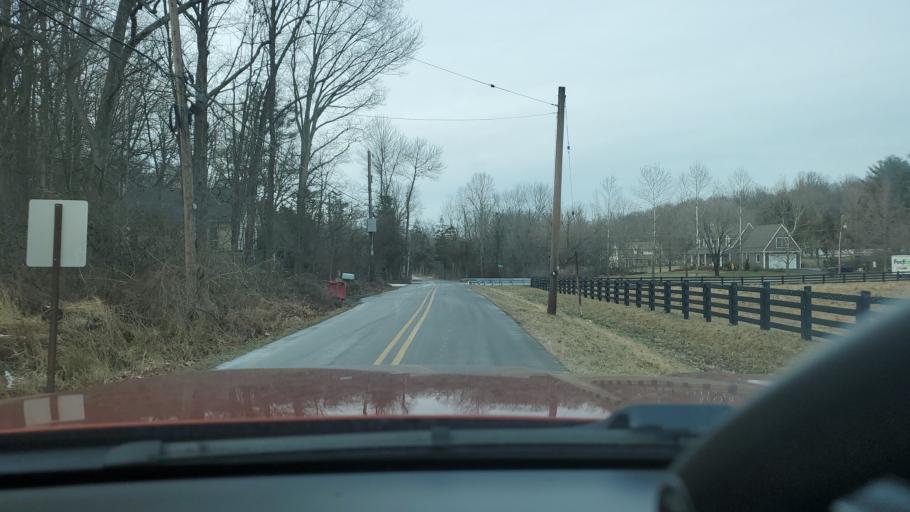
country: US
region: Pennsylvania
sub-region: Montgomery County
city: Woxall
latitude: 40.3189
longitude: -75.5001
